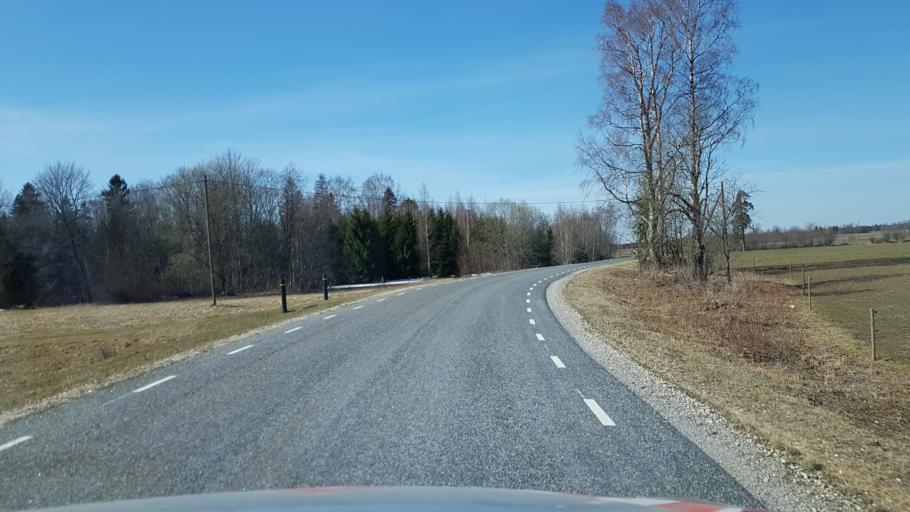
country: EE
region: Laeaene-Virumaa
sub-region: Vinni vald
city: Vinni
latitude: 59.0949
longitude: 26.5030
